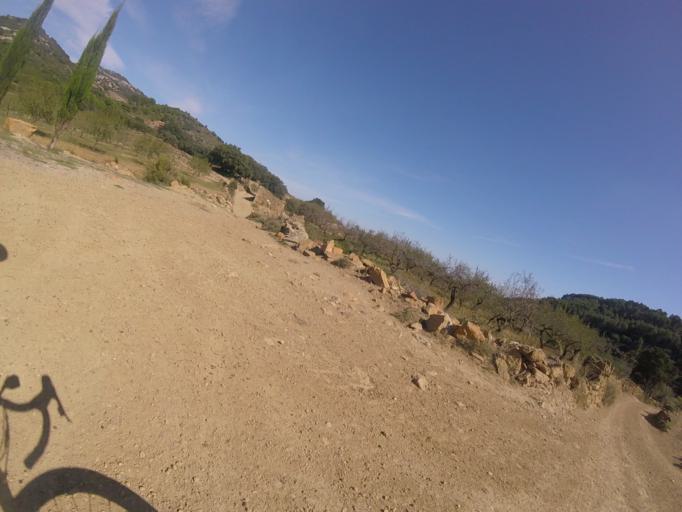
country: ES
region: Valencia
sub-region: Provincia de Castello
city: Sierra-Engarceran
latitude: 40.2735
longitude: -0.0052
